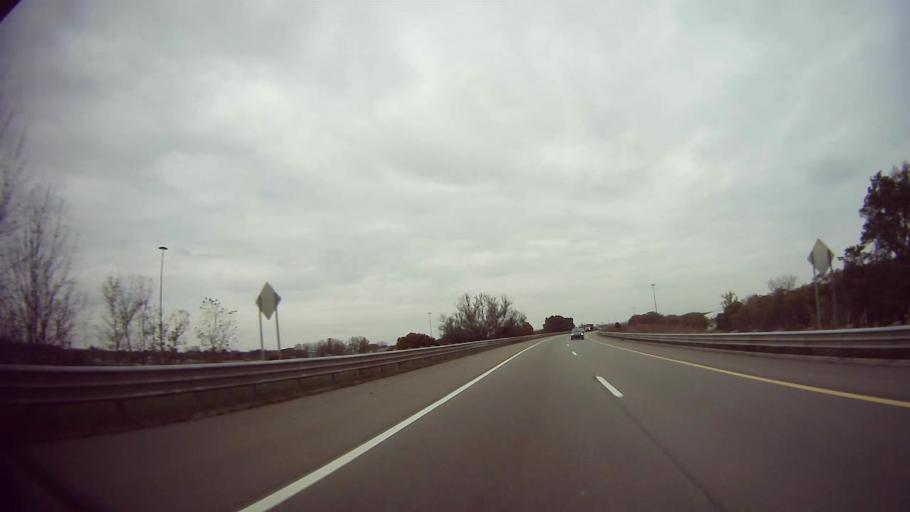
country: US
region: Michigan
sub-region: Wayne County
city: Plymouth
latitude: 42.3879
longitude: -83.4332
